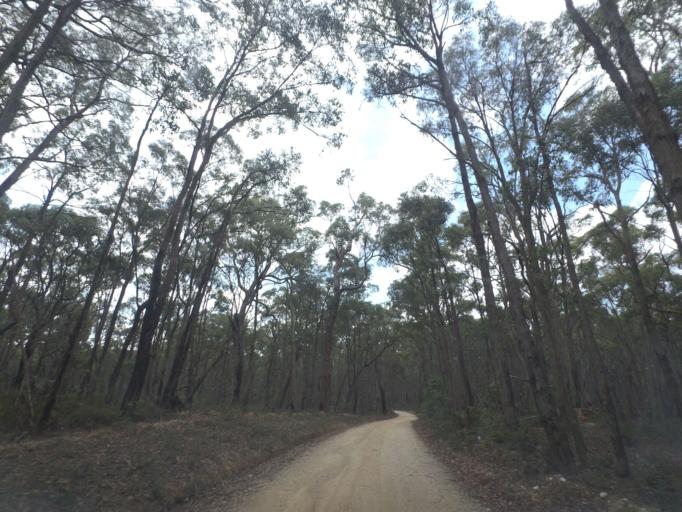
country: AU
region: Victoria
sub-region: Moorabool
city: Bacchus Marsh
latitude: -37.4969
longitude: 144.4331
